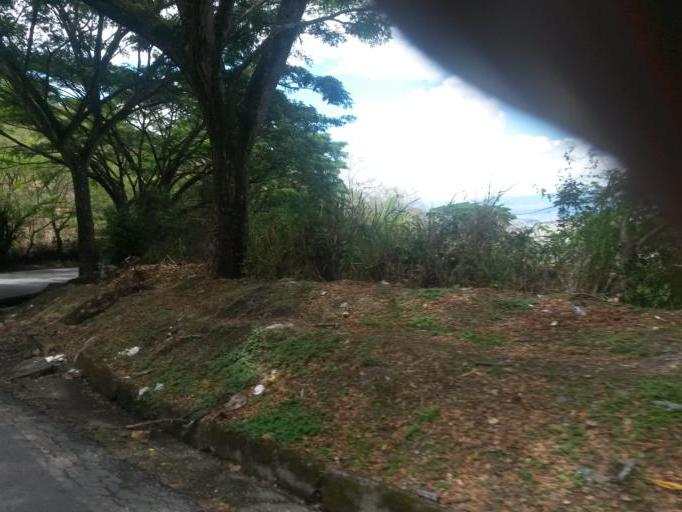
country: CO
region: Cauca
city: El Bordo
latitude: 2.1058
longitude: -76.9902
